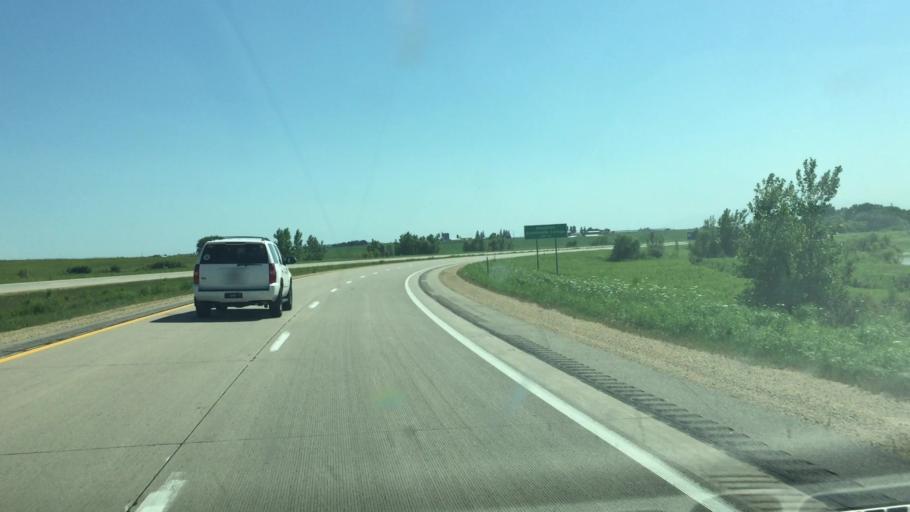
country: US
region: Iowa
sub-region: Jones County
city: Monticello
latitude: 42.2112
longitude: -91.1747
